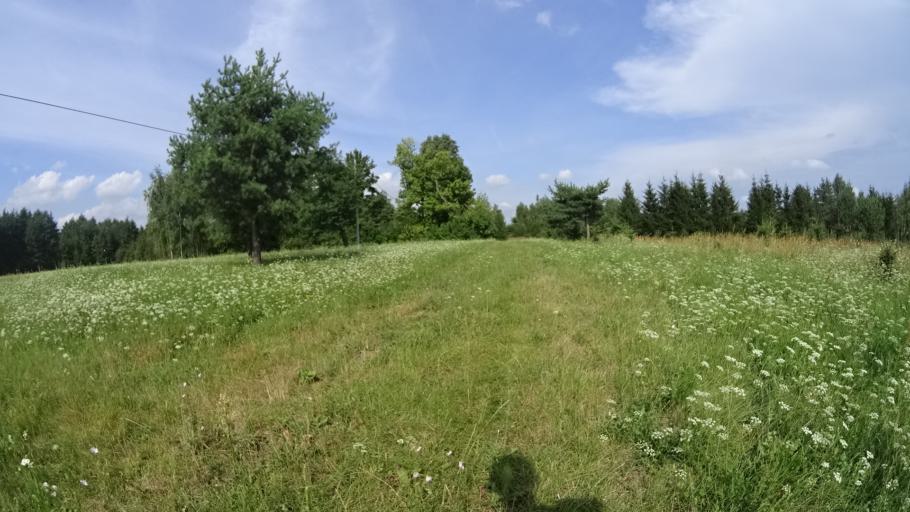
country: PL
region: Masovian Voivodeship
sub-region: Powiat grojecki
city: Goszczyn
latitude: 51.6932
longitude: 20.8341
